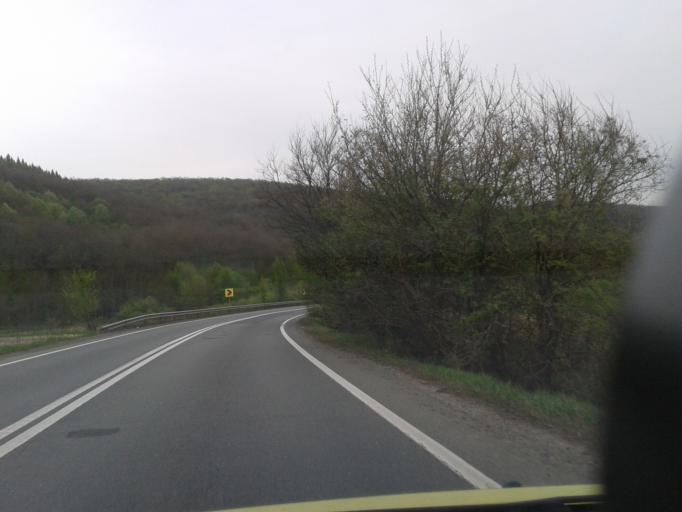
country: RO
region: Arad
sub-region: Comuna Barzava
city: Barzava
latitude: 46.1117
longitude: 21.9530
